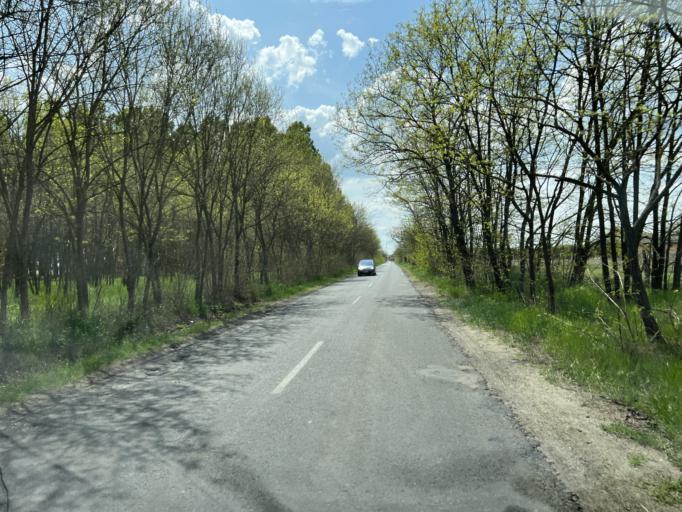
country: HU
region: Pest
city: Csemo
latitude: 47.1237
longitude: 19.7038
